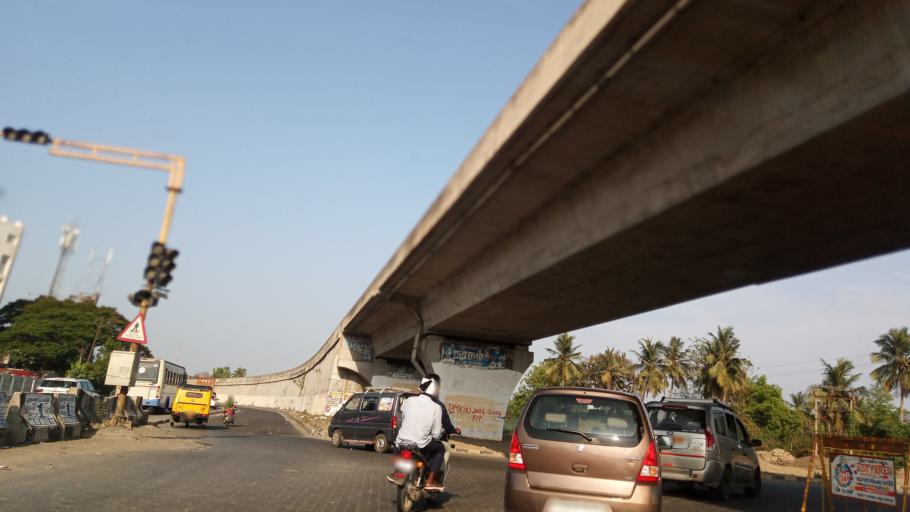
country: IN
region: Tamil Nadu
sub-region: Kancheepuram
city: Poonamalle
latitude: 13.0548
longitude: 80.1238
